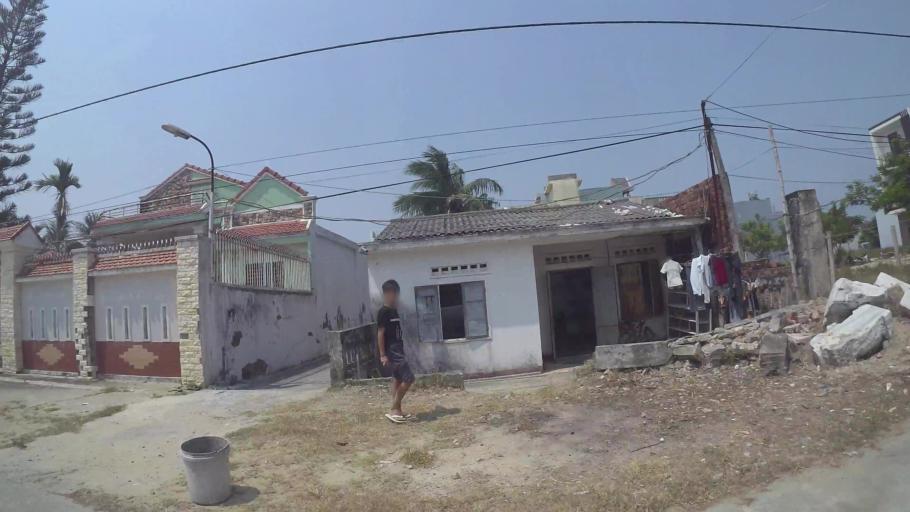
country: VN
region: Da Nang
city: Ngu Hanh Son
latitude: 15.9940
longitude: 108.2671
